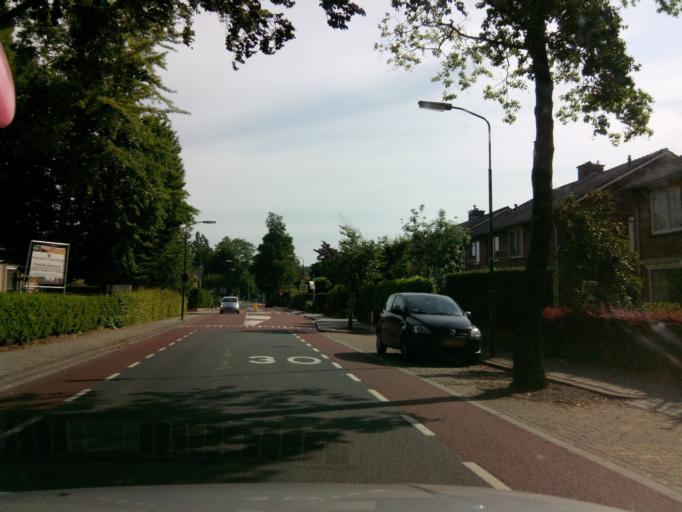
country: NL
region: Utrecht
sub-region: Gemeente Bunnik
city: Bunnik
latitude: 52.0660
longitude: 5.2057
